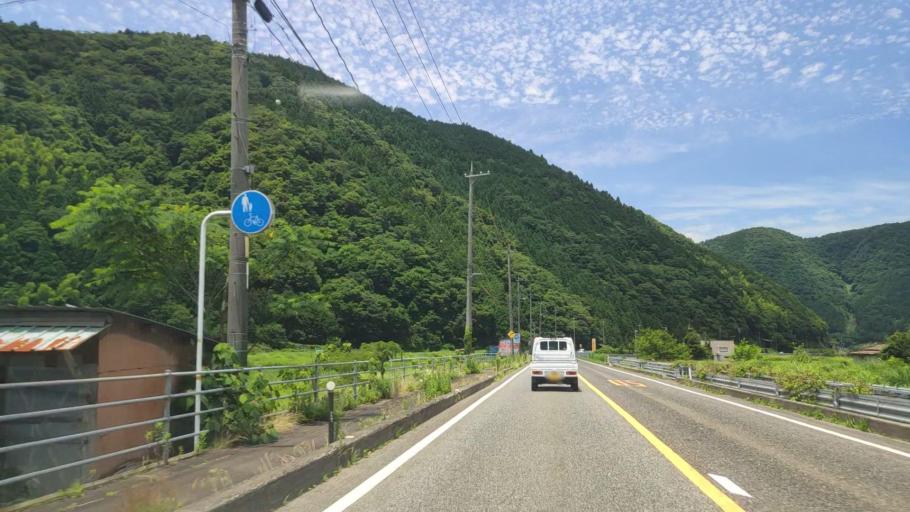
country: JP
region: Tottori
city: Tottori
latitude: 35.3588
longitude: 134.3799
